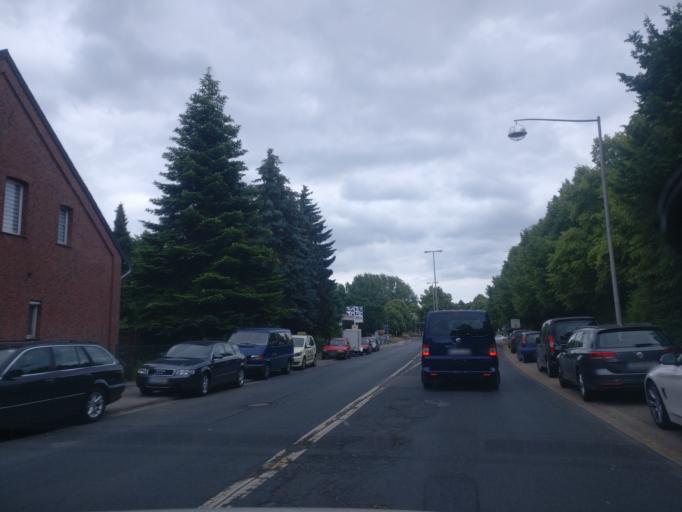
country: DE
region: Lower Saxony
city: Laatzen
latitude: 52.3568
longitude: 9.8273
